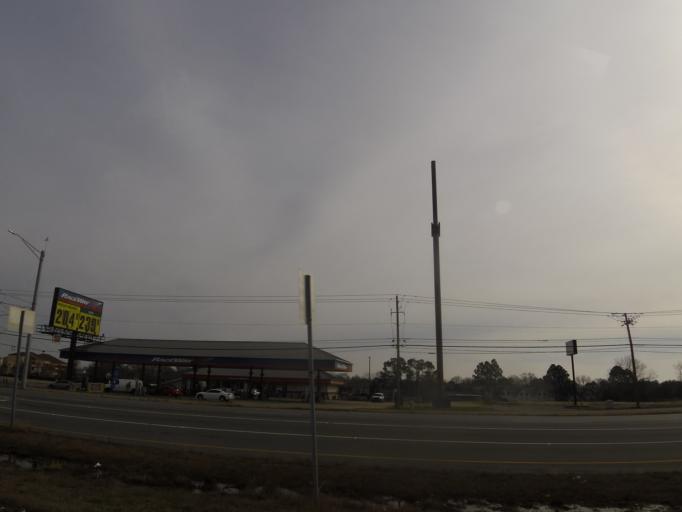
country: US
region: Alabama
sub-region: Montgomery County
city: Montgomery
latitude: 32.3597
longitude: -86.2155
